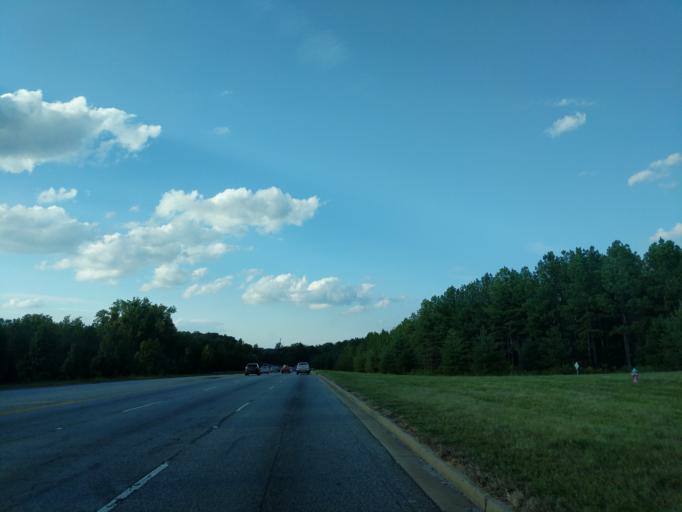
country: US
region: South Carolina
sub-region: Greenville County
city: Greer
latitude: 34.8851
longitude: -82.2319
